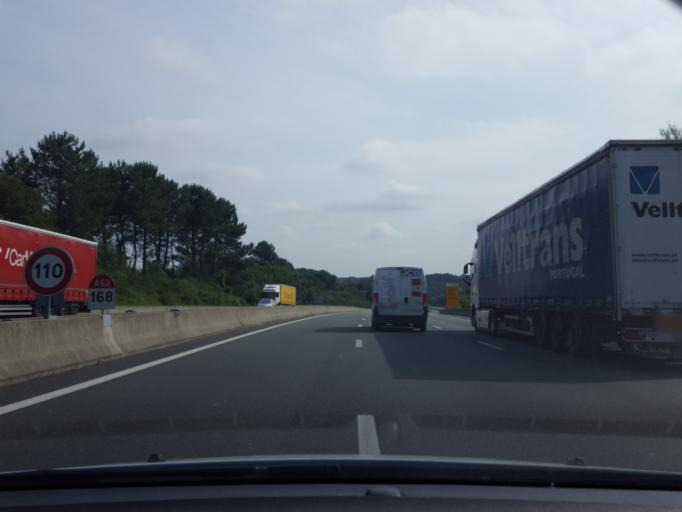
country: FR
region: Aquitaine
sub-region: Departement des Pyrenees-Atlantiques
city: Boucau
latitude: 43.5260
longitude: -1.4388
